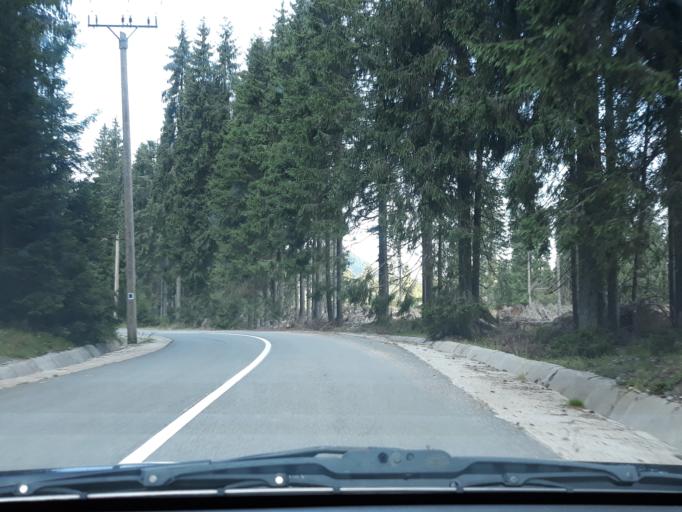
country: RO
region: Alba
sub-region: Comuna Arieseni
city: Arieseni
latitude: 46.5960
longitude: 22.7233
